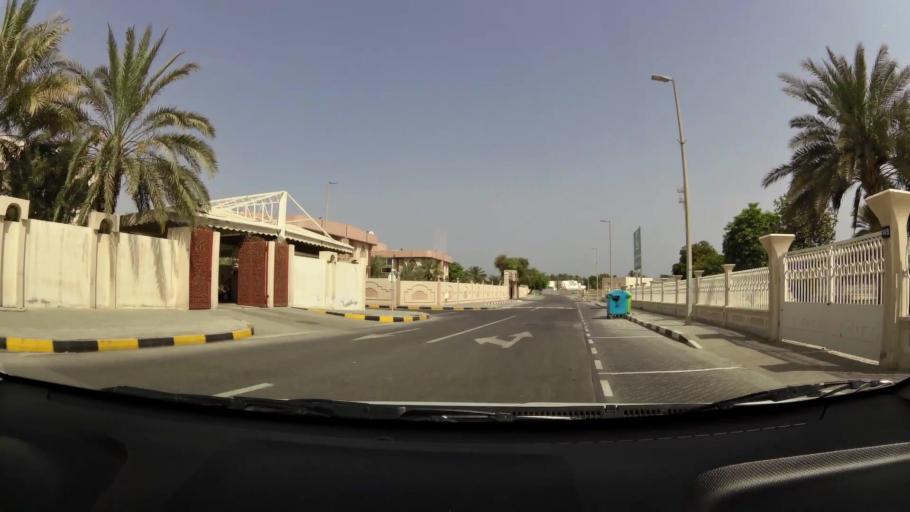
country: AE
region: Ash Shariqah
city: Sharjah
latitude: 25.3507
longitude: 55.4181
